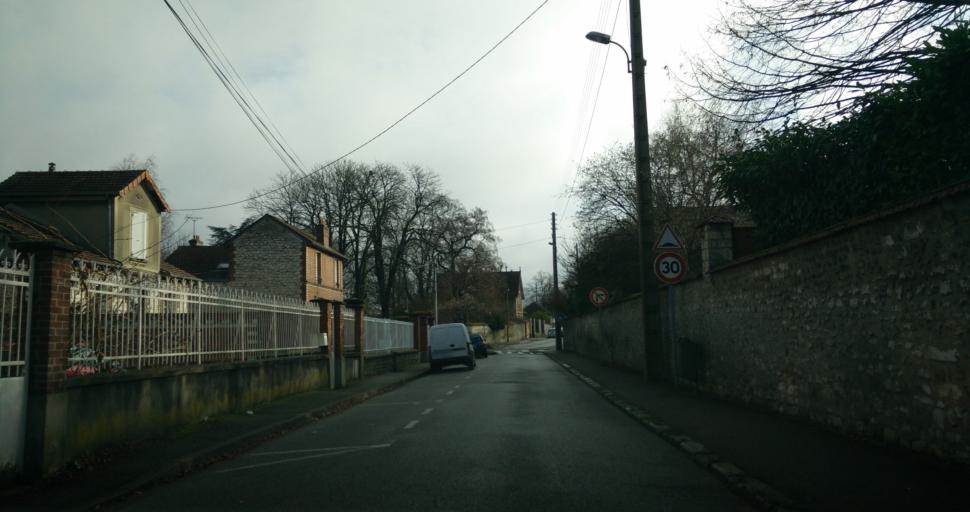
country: FR
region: Haute-Normandie
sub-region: Departement de l'Eure
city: Vernon
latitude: 49.0953
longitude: 1.4784
